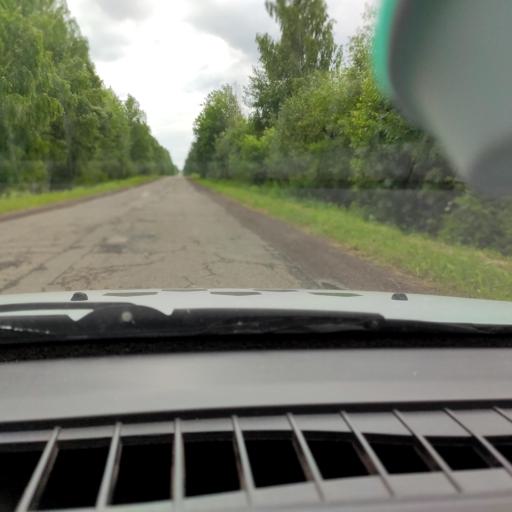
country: RU
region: Perm
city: Kukushtan
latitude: 57.2821
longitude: 56.5356
